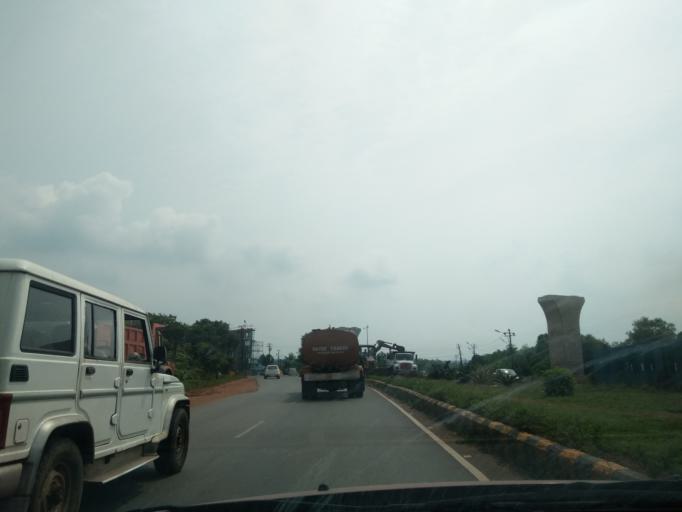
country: IN
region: Goa
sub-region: North Goa
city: Panaji
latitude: 15.4919
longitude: 73.8433
